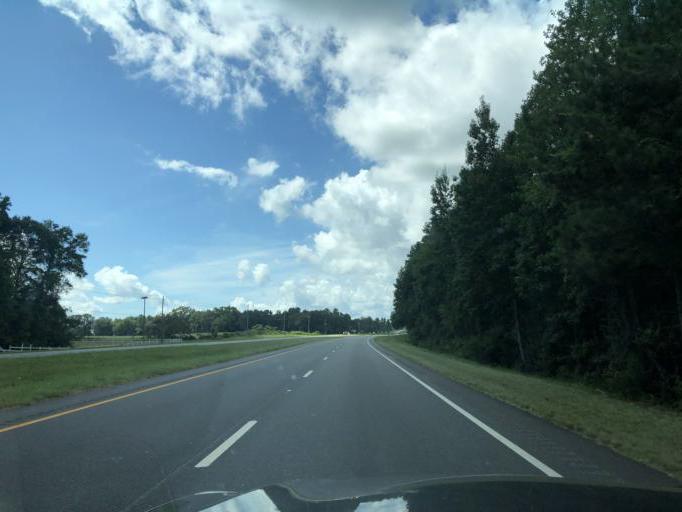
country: US
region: Alabama
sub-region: Barbour County
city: Eufaula
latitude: 31.9597
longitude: -85.1193
